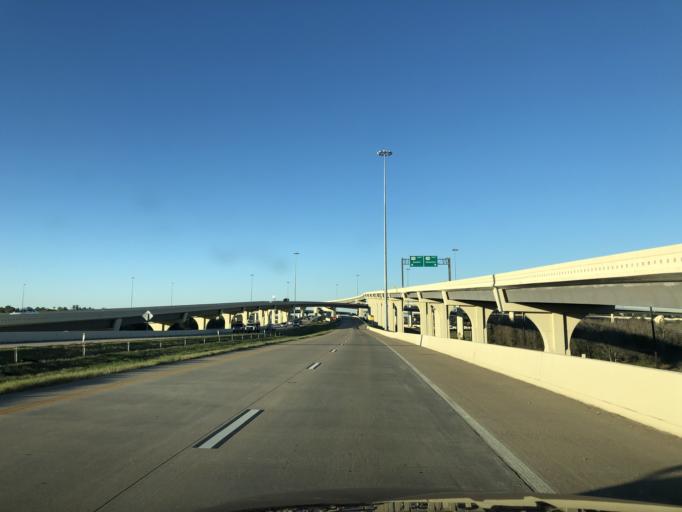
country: US
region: Texas
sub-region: Harris County
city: Cypress
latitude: 29.9934
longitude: -95.7688
